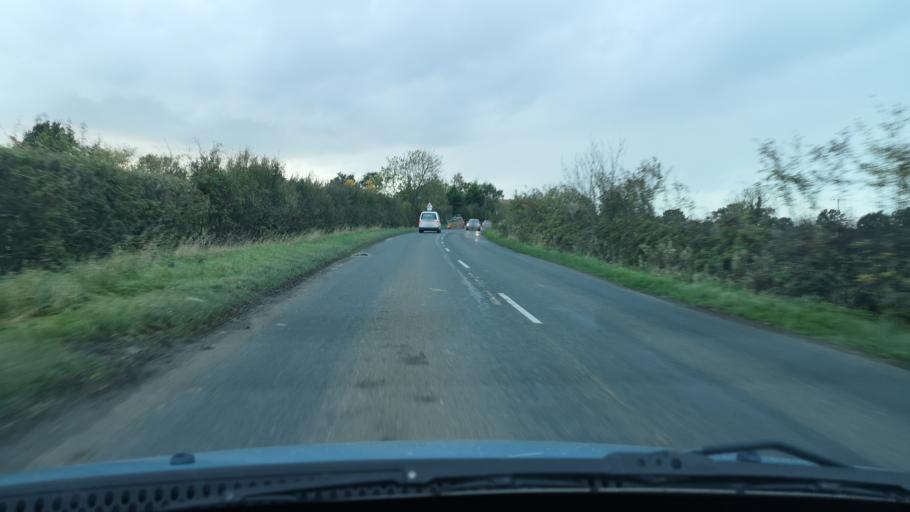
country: GB
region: England
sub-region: Doncaster
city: Moss
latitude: 53.6220
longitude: -1.1067
